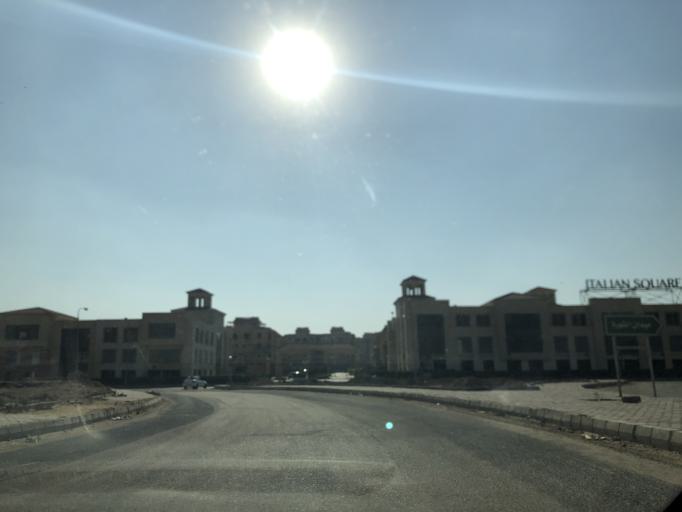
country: EG
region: Al Jizah
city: Madinat Sittah Uktubar
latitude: 29.9137
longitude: 31.0657
